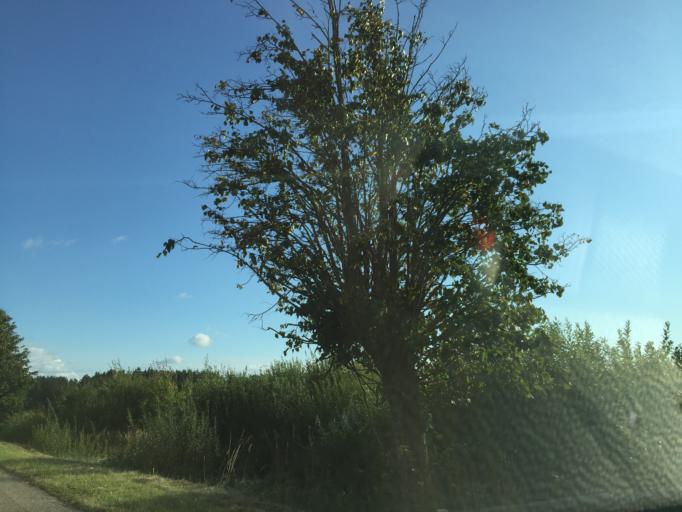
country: LV
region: Krimulda
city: Ragana
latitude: 57.2246
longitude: 24.6943
